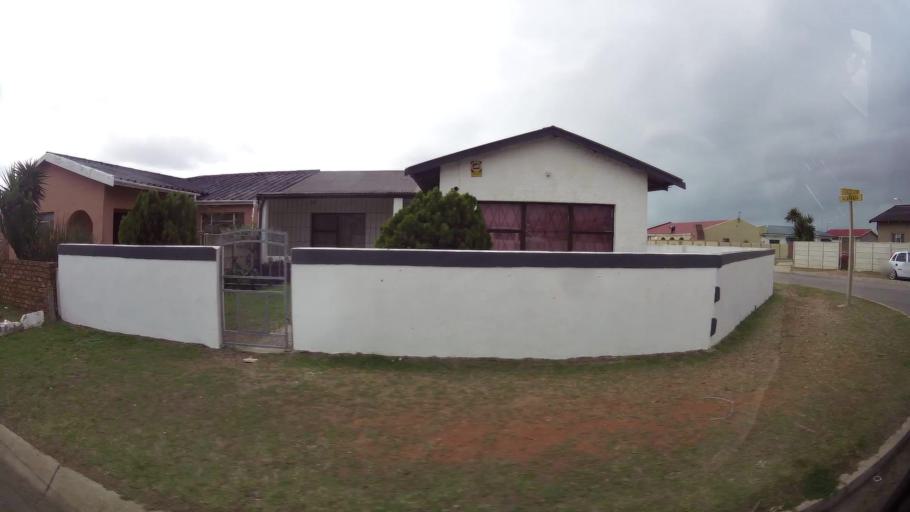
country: ZA
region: Eastern Cape
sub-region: Nelson Mandela Bay Metropolitan Municipality
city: Port Elizabeth
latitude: -33.8975
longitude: 25.5644
